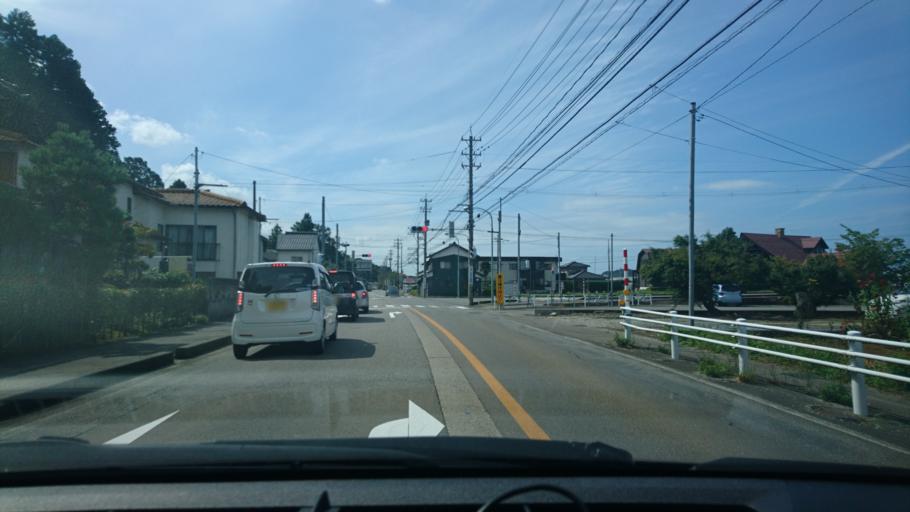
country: JP
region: Ishikawa
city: Komatsu
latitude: 36.3070
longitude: 136.3339
